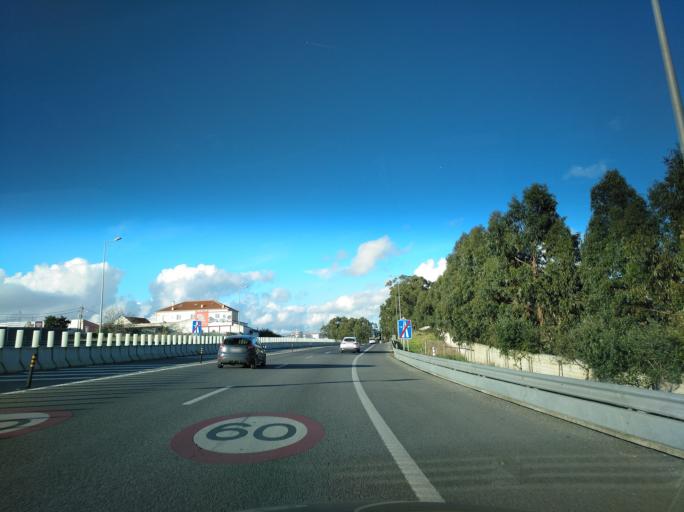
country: PT
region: Setubal
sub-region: Almada
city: Sobreda
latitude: 38.6523
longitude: -9.2010
